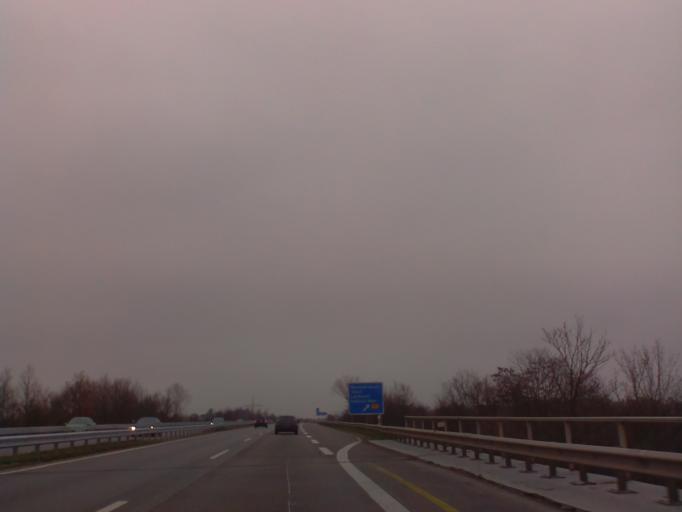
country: DE
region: Rheinland-Pfalz
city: Lachen-Speyerdorf
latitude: 49.3576
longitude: 8.1959
